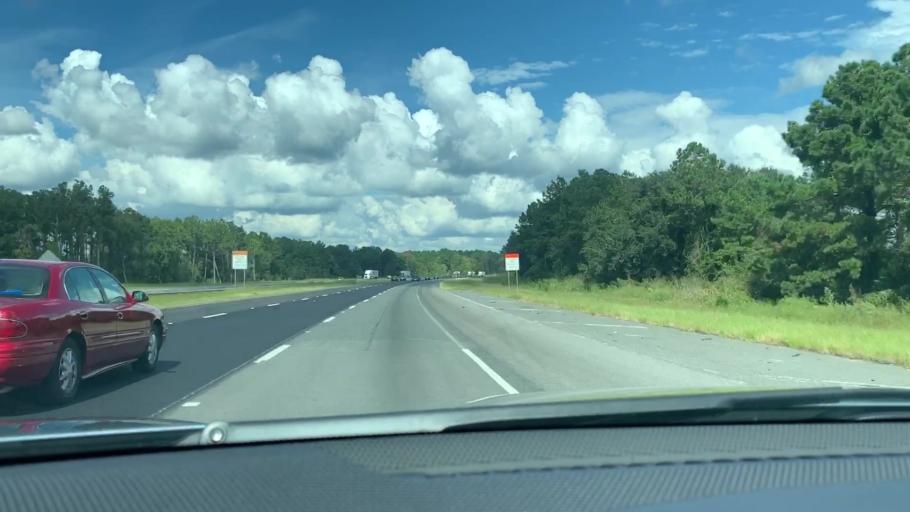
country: US
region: Georgia
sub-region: Camden County
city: Woodbine
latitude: 31.0410
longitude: -81.6510
